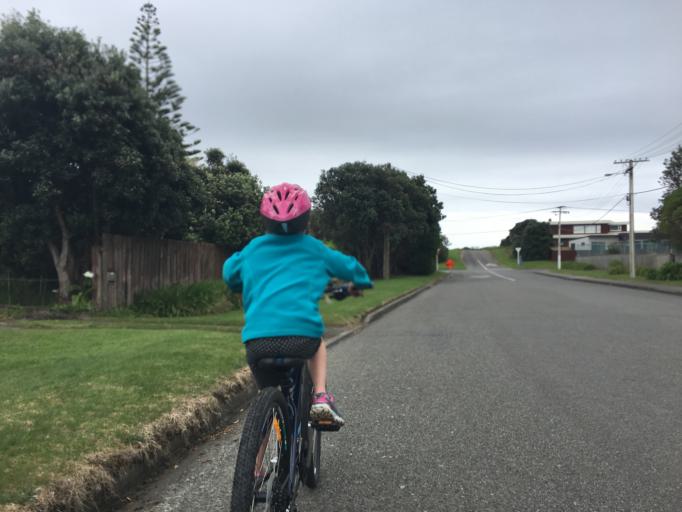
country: NZ
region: Wellington
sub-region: Kapiti Coast District
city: Paraparaumu
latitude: -40.8646
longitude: 175.0211
